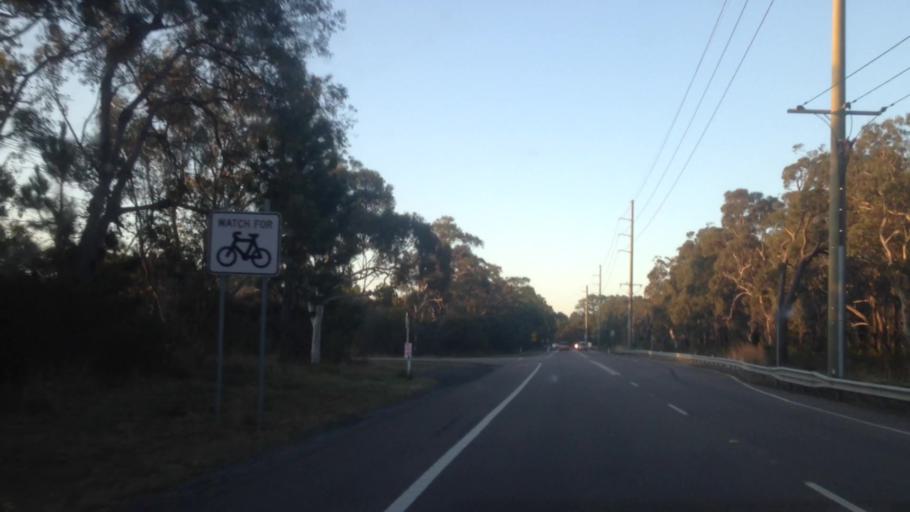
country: AU
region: New South Wales
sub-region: Wyong Shire
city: Kingfisher Shores
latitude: -33.1805
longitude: 151.5390
